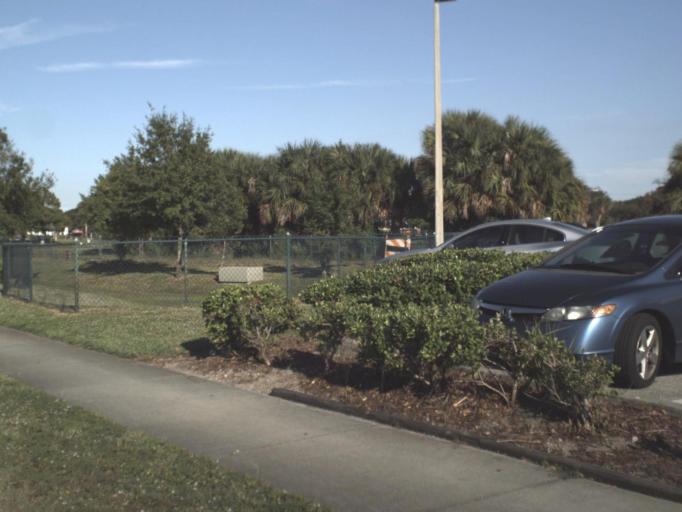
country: US
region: Florida
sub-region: Brevard County
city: June Park
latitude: 28.1201
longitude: -80.6722
